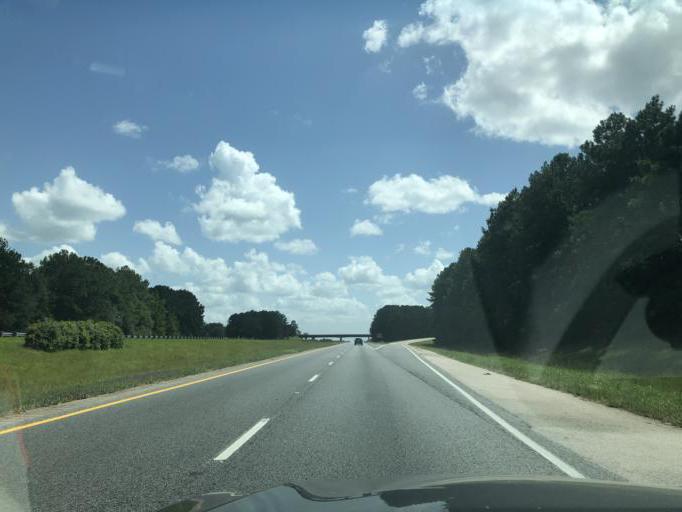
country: US
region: Georgia
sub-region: Troup County
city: La Grange
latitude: 32.9673
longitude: -84.9558
